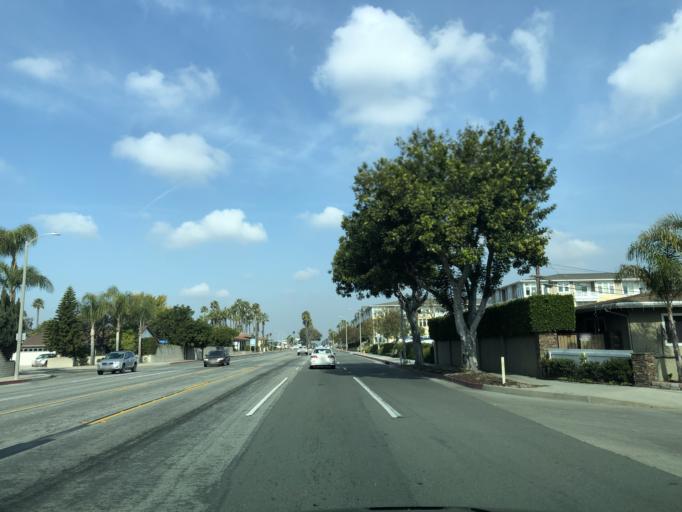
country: US
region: California
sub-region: Orange County
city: Midway City
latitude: 33.7114
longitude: -118.0065
